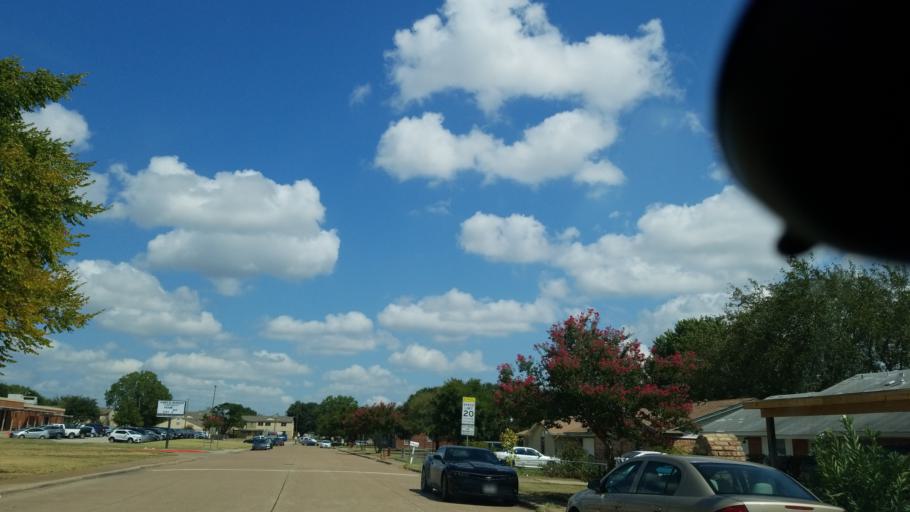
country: US
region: Texas
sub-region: Dallas County
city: Grand Prairie
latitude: 32.7174
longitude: -96.9871
